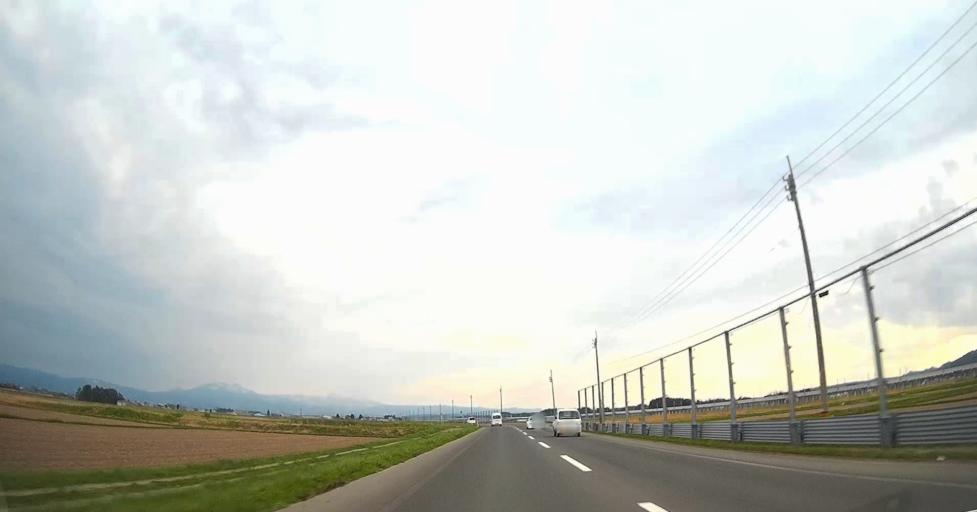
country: JP
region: Aomori
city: Aomori Shi
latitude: 40.8795
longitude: 140.6710
